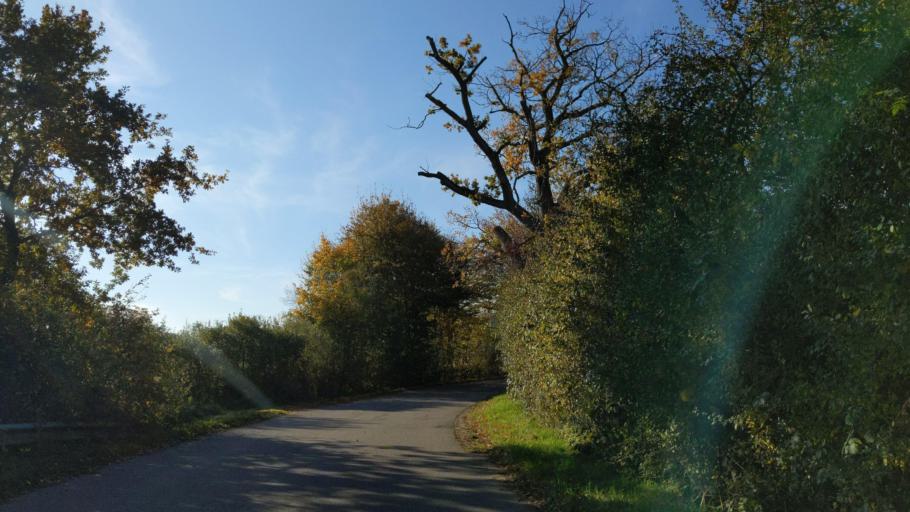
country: DE
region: Schleswig-Holstein
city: Kasseedorf
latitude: 54.1342
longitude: 10.7325
